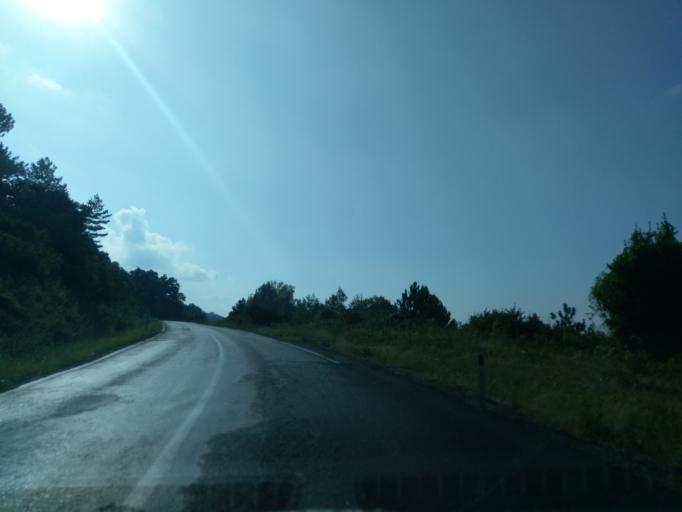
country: TR
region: Sinop
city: Yenikonak
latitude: 41.9429
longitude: 34.7034
